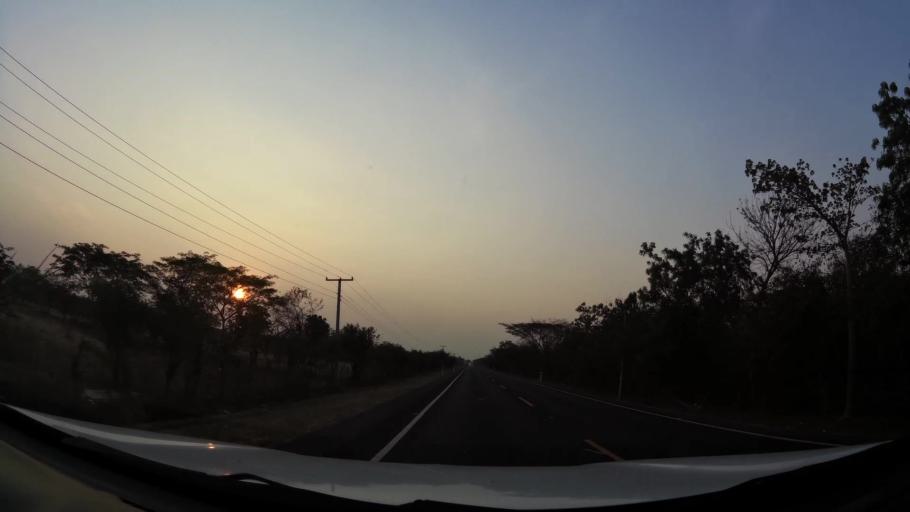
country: NI
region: Leon
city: La Paz Centro
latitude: 12.3160
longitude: -86.7896
